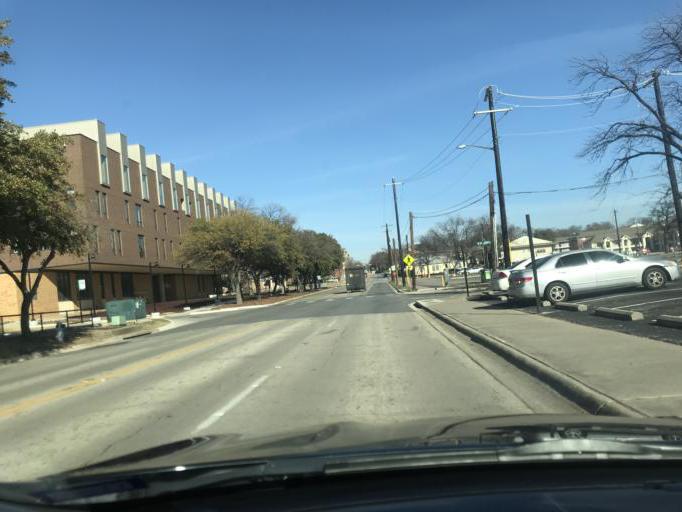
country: US
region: Texas
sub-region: Denton County
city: Denton
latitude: 33.2122
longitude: -97.1443
